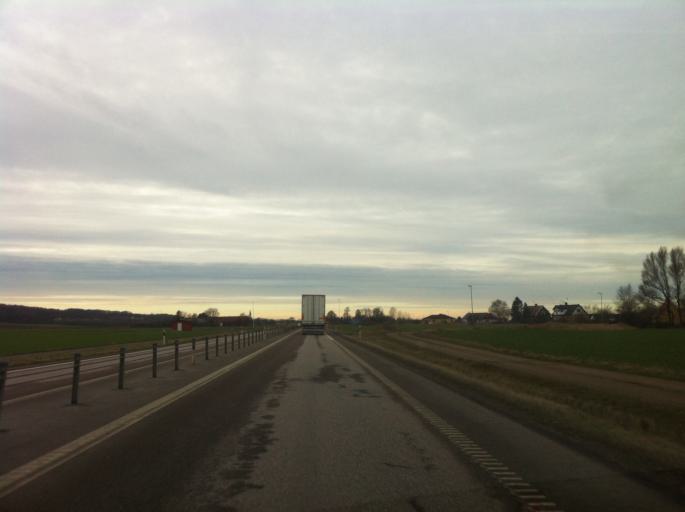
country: SE
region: Skane
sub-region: Astorps Kommun
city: Kvidinge
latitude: 56.1355
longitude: 13.0096
